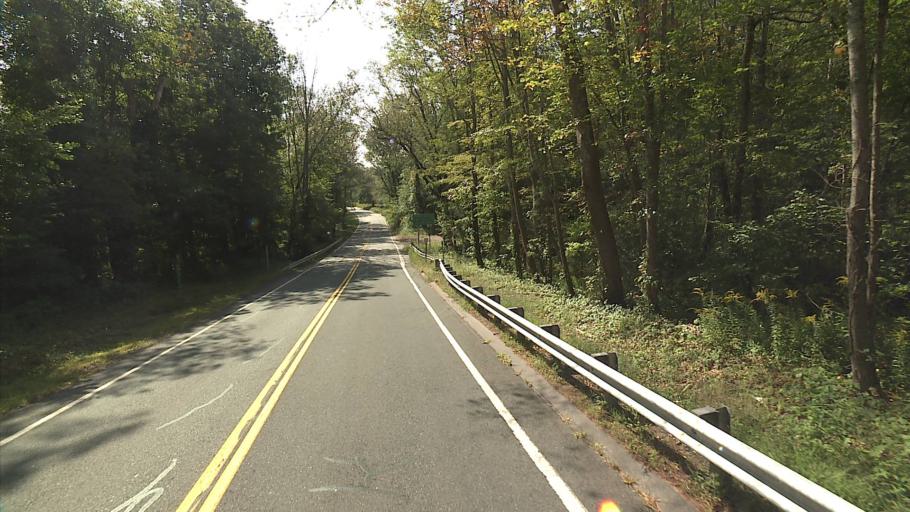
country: US
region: Massachusetts
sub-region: Worcester County
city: Southbridge
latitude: 42.0274
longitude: -72.0101
